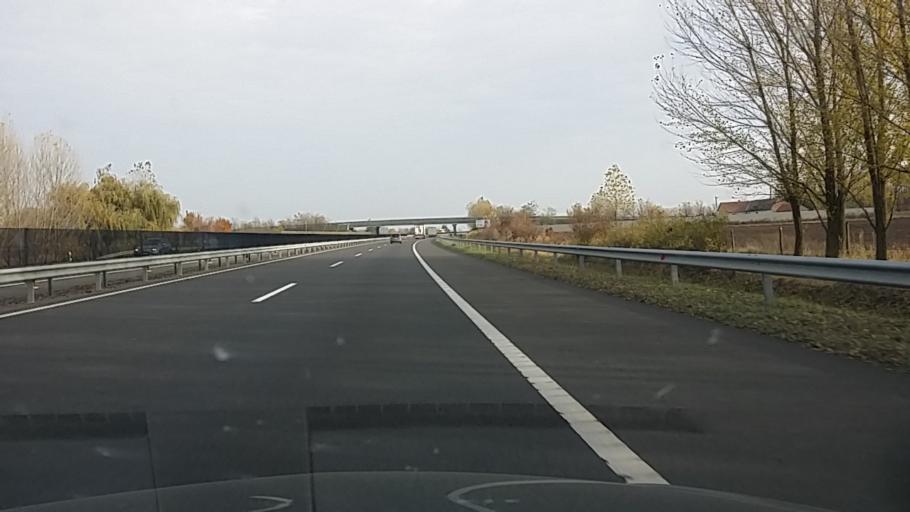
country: HU
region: Szabolcs-Szatmar-Bereg
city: Nyiregyhaza
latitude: 47.9019
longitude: 21.6628
